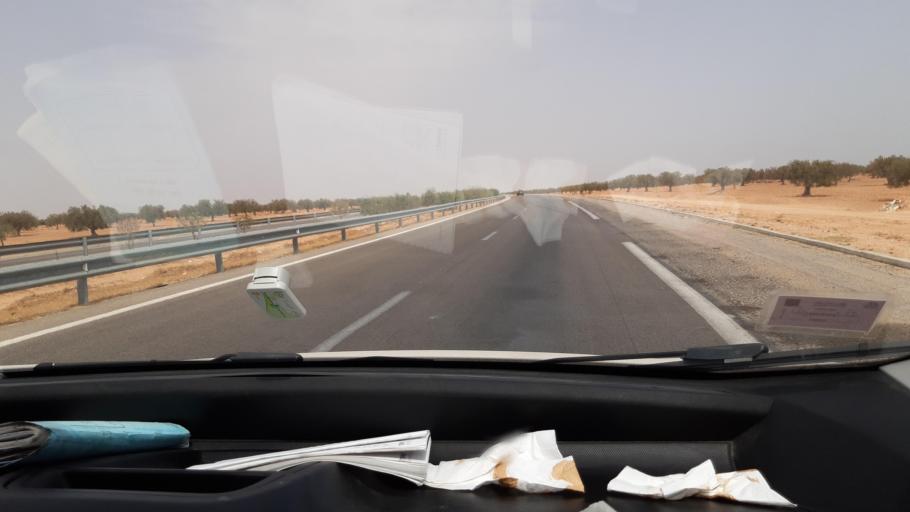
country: TN
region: Safaqis
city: Bi'r `Ali Bin Khalifah
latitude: 34.5680
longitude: 10.3755
